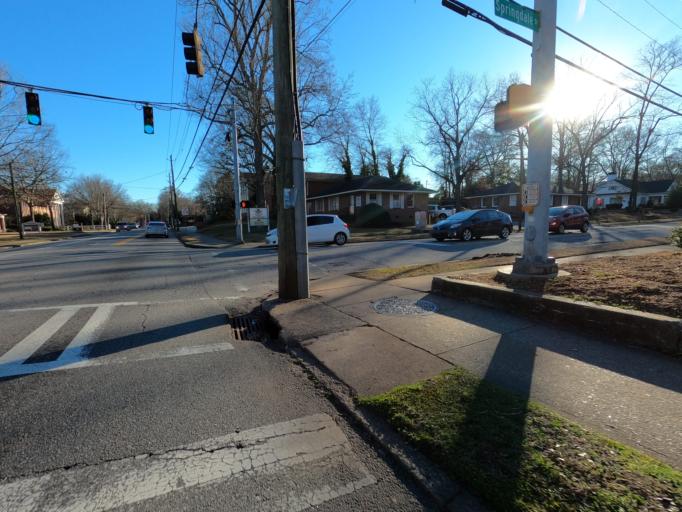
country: US
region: Georgia
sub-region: Clarke County
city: Athens
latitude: 33.9461
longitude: -83.3878
